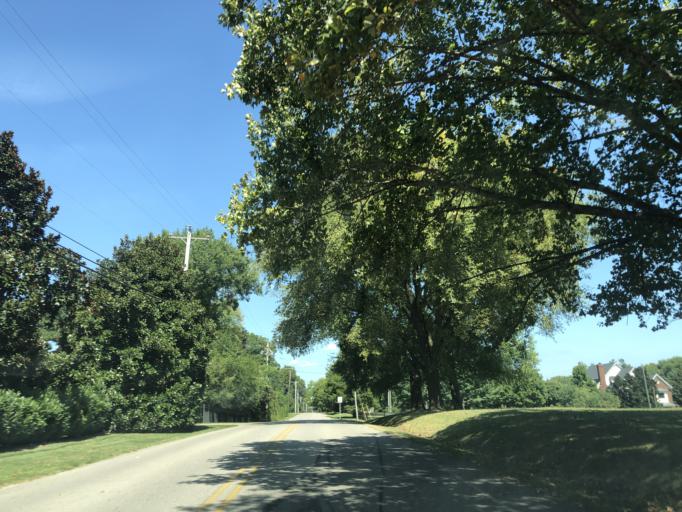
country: US
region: Tennessee
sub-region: Davidson County
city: Oak Hill
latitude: 36.0804
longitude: -86.7918
